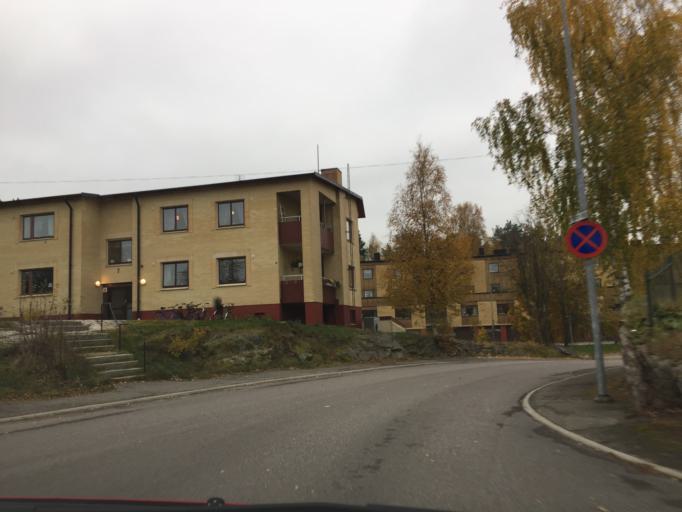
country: SE
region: Vaestra Goetaland
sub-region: Trollhattan
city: Trollhattan
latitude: 58.2612
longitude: 12.2711
